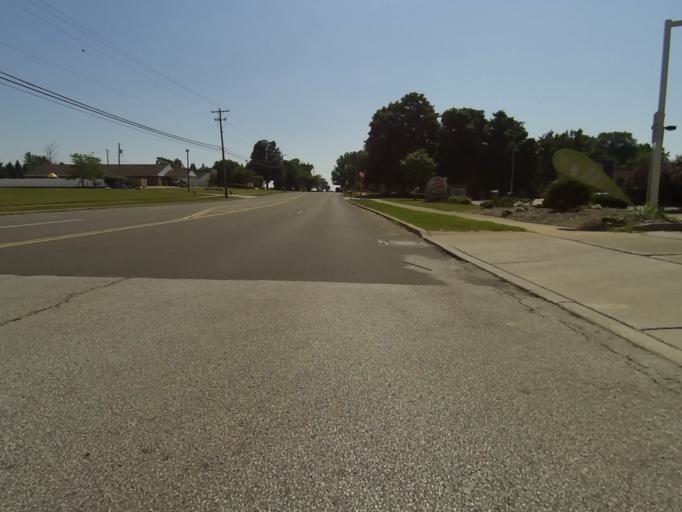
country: US
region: Ohio
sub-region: Summit County
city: Stow
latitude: 41.1664
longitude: -81.4037
